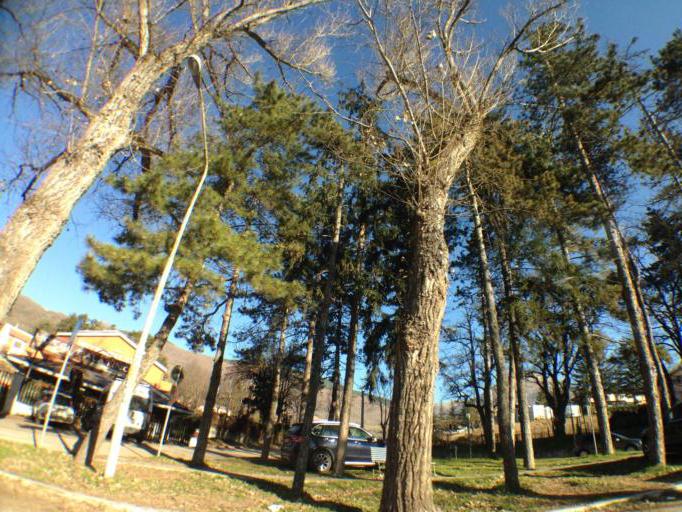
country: IT
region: Umbria
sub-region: Provincia di Perugia
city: Norcia
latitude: 42.7959
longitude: 13.0913
